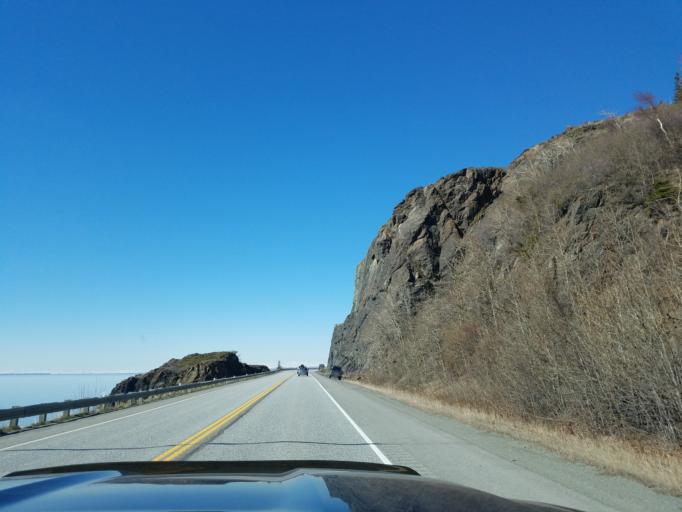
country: US
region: Alaska
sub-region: Anchorage Municipality
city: Anchorage
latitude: 61.0349
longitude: -149.7736
